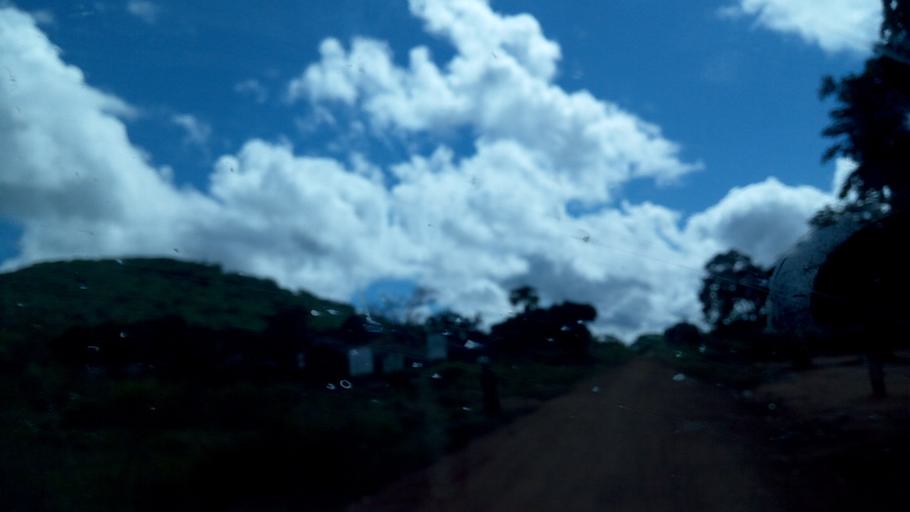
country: ZM
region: Northern
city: Kaputa
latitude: -8.2188
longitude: 29.0566
